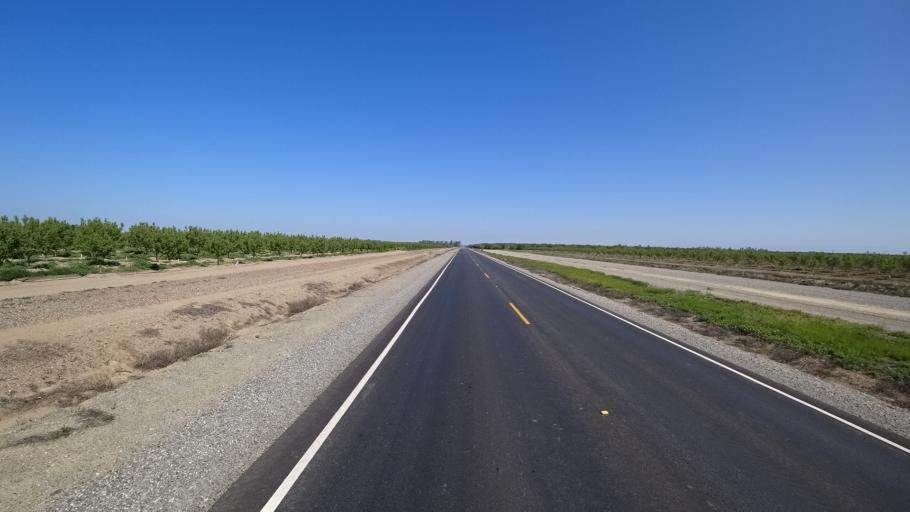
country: US
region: California
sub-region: Glenn County
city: Hamilton City
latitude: 39.6442
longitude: -122.0650
